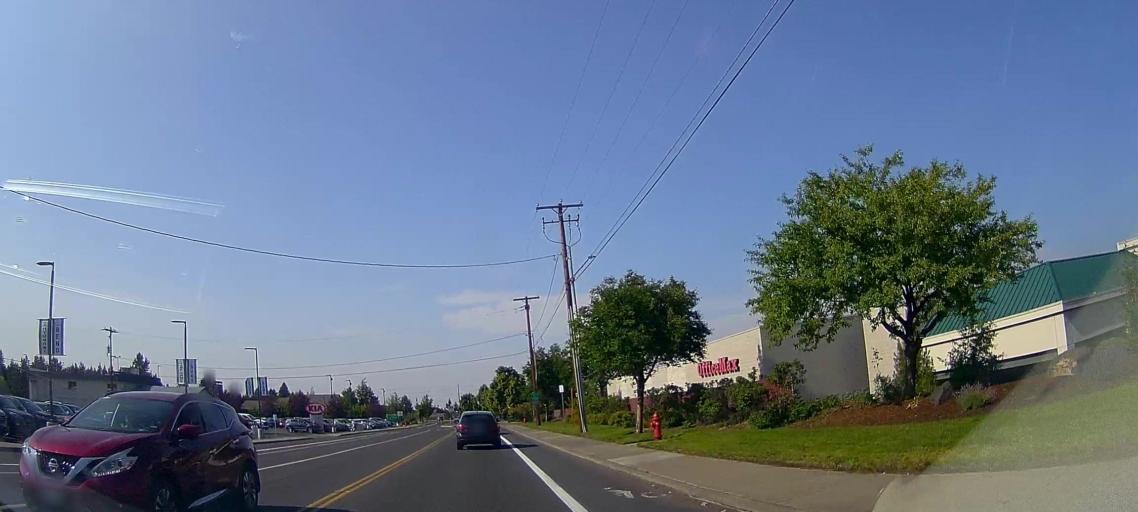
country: US
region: Oregon
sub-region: Deschutes County
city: Bend
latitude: 44.0552
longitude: -121.2686
